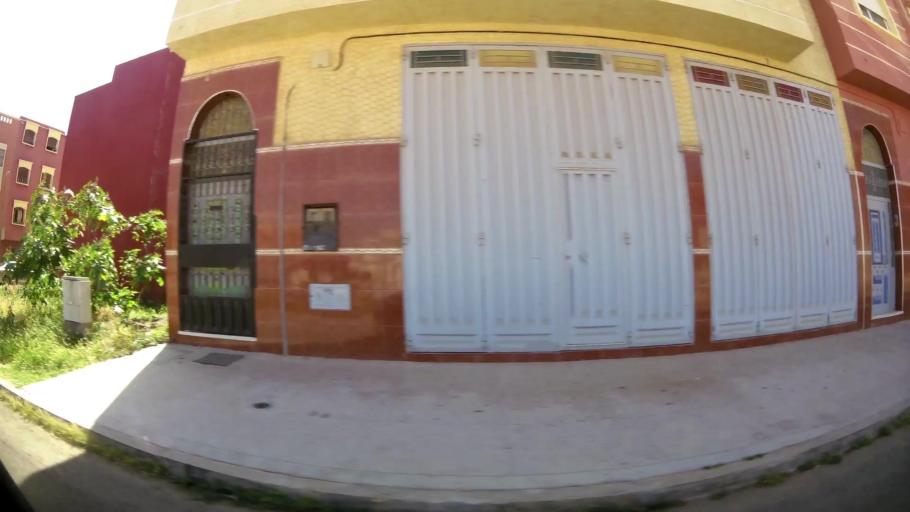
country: MA
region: Souss-Massa-Draa
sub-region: Inezgane-Ait Mellou
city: Inezgane
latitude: 30.3297
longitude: -9.5091
